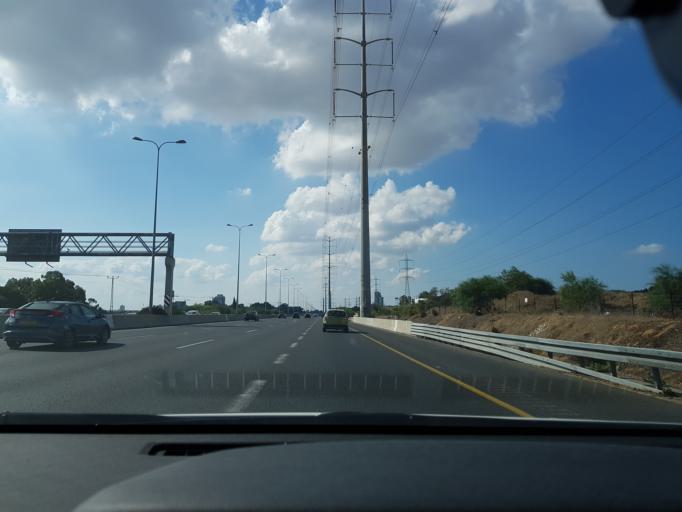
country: IL
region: Central District
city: Rishon LeZiyyon
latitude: 31.9925
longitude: 34.7985
